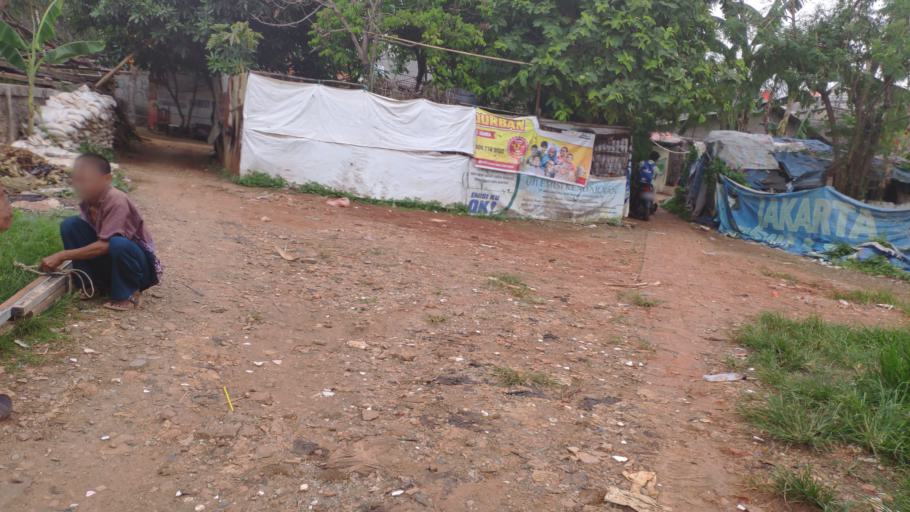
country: ID
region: Jakarta Raya
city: Jakarta
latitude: -6.2672
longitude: 106.8261
